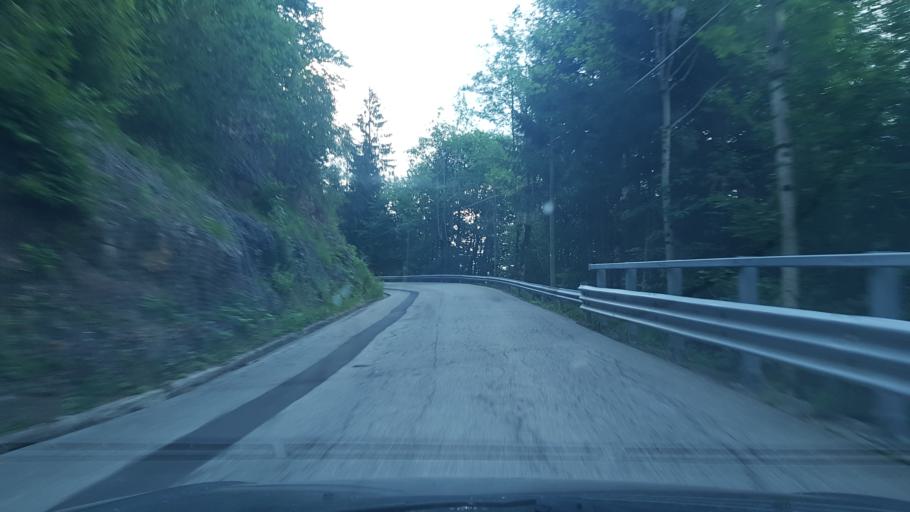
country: IT
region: Friuli Venezia Giulia
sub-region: Provincia di Udine
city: Forni Avoltri
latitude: 46.5863
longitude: 12.7827
